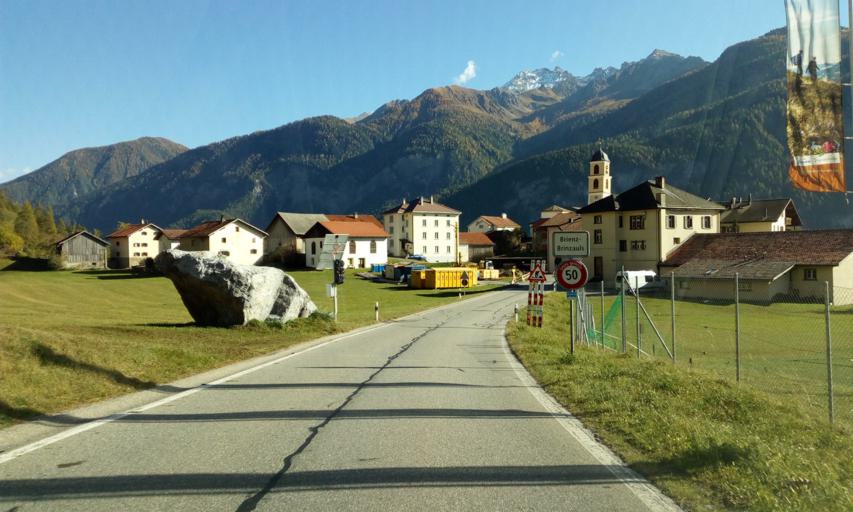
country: CH
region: Grisons
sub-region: Albula District
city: Tiefencastel
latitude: 46.6704
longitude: 9.5934
